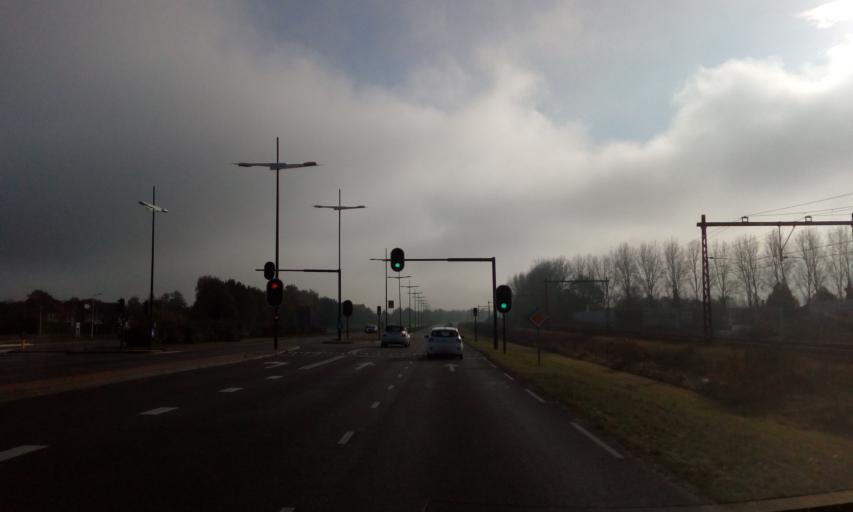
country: NL
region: Overijssel
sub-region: Gemeente Deventer
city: Schalkhaar
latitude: 52.2476
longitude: 6.2019
